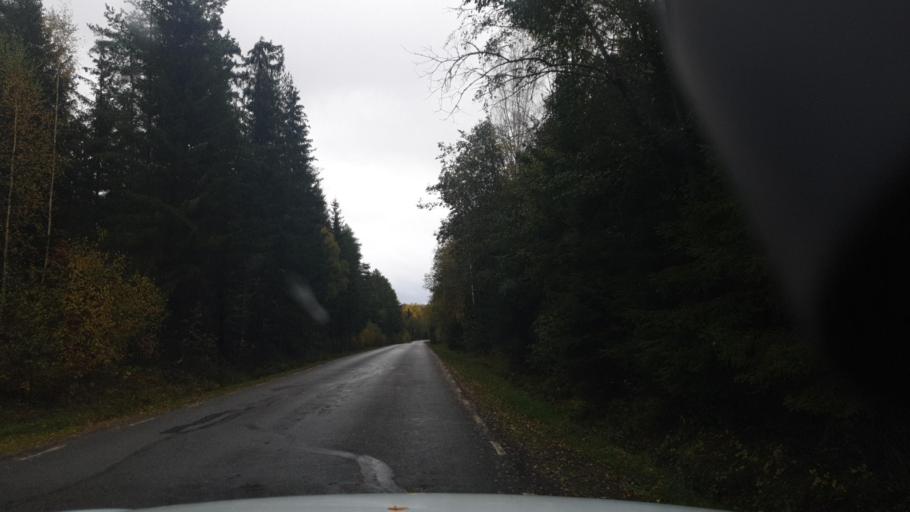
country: SE
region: Vaermland
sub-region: Karlstads Kommun
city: Valberg
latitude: 59.4125
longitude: 13.1699
